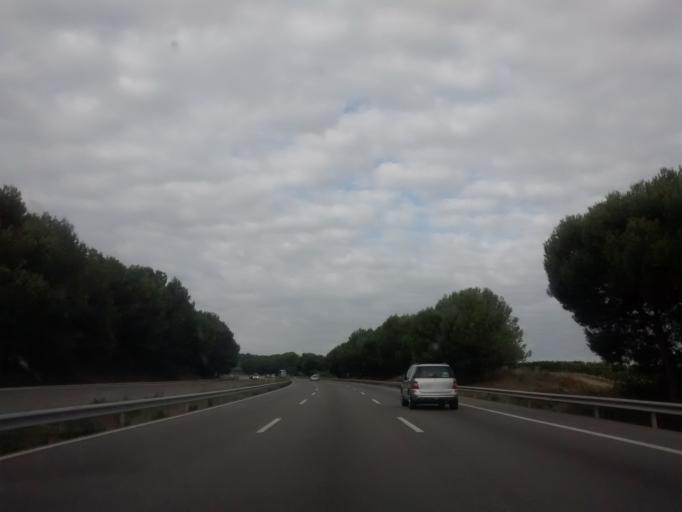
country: ES
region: Catalonia
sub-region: Provincia de Barcelona
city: Sant Sadurni d'Anoia
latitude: 41.3936
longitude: 1.7658
